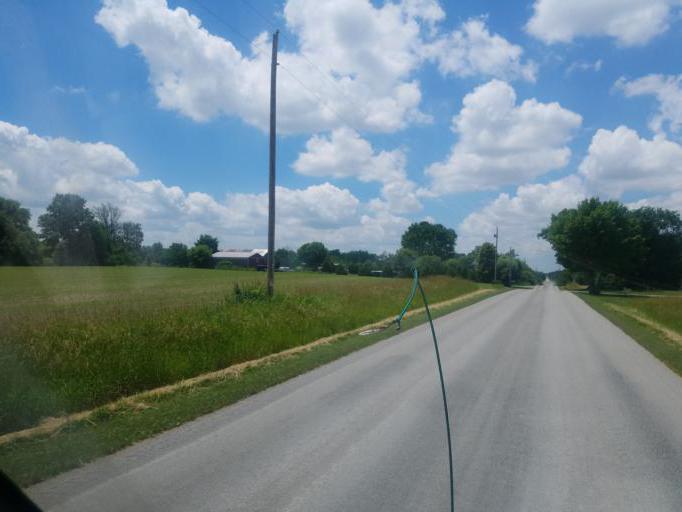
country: US
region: Ohio
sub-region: Huron County
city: Willard
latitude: 41.0792
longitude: -82.7124
